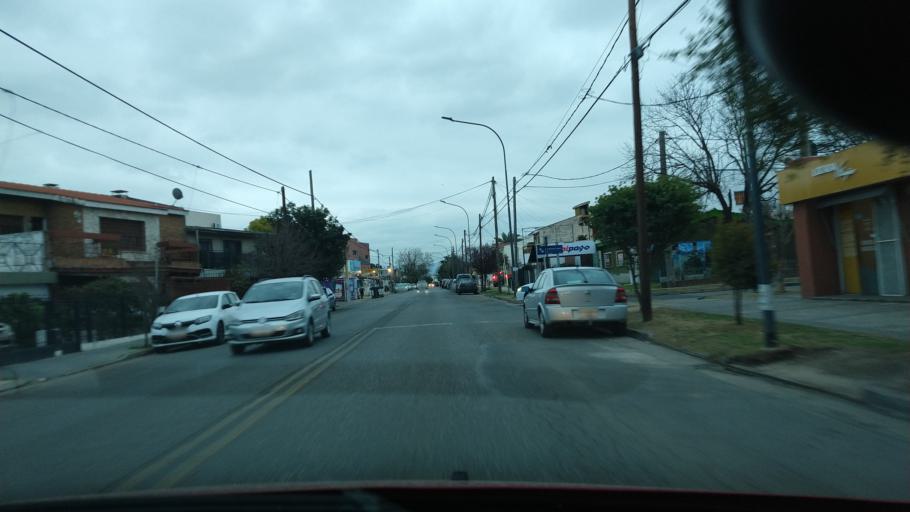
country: AR
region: Cordoba
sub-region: Departamento de Capital
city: Cordoba
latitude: -31.3604
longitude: -64.2335
